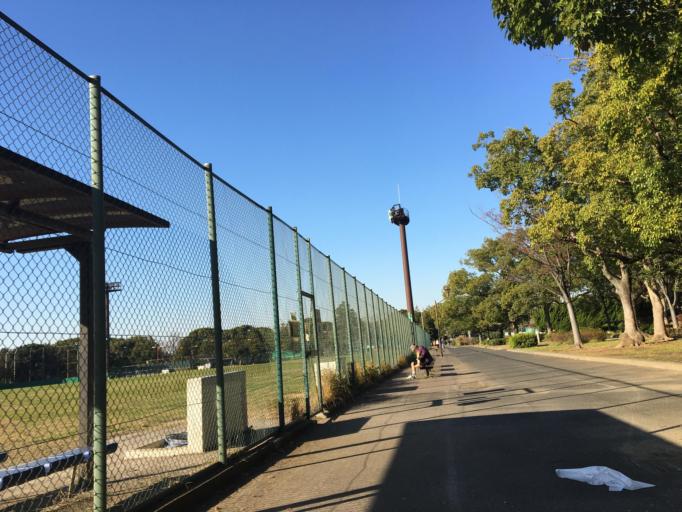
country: JP
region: Tokyo
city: Urayasu
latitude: 35.7146
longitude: 139.8994
